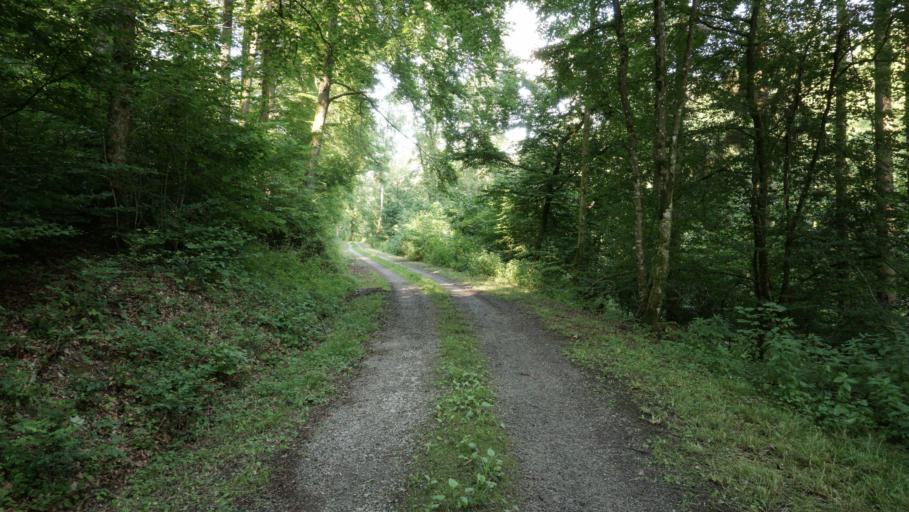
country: DE
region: Baden-Wuerttemberg
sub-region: Karlsruhe Region
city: Fahrenbach
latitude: 49.4213
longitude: 9.1105
